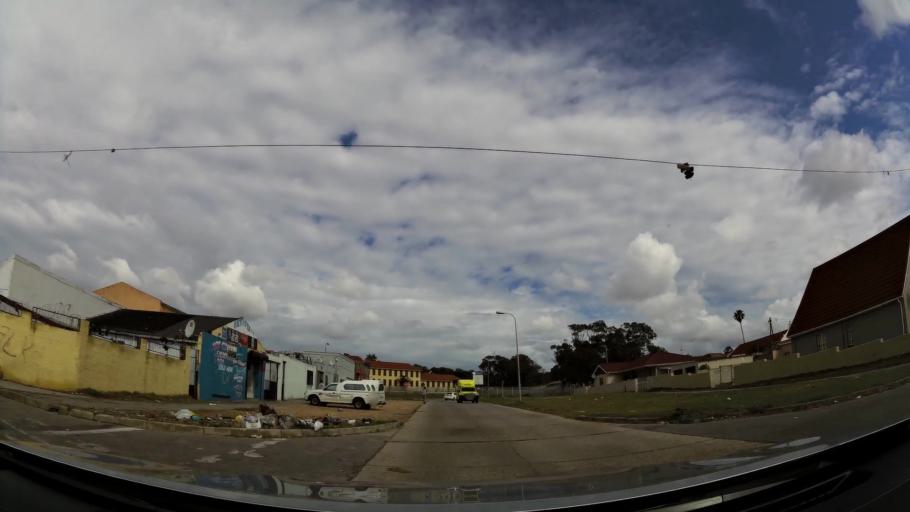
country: ZA
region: Eastern Cape
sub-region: Nelson Mandela Bay Metropolitan Municipality
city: Port Elizabeth
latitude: -33.9304
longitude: 25.5730
